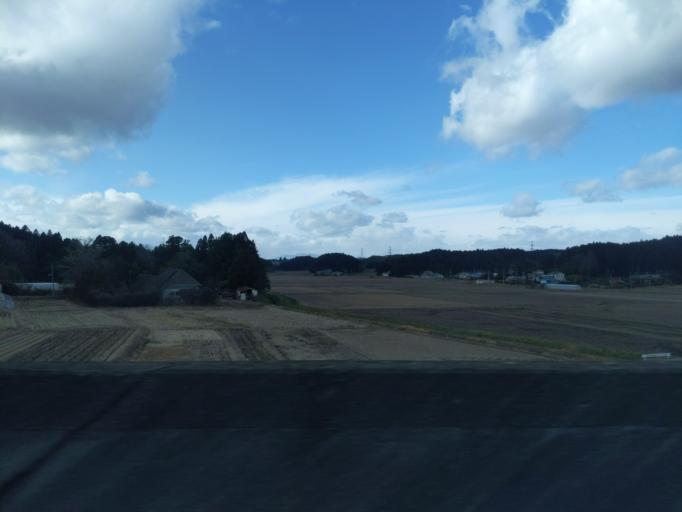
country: JP
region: Miyagi
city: Furukawa
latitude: 38.6233
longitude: 140.9988
